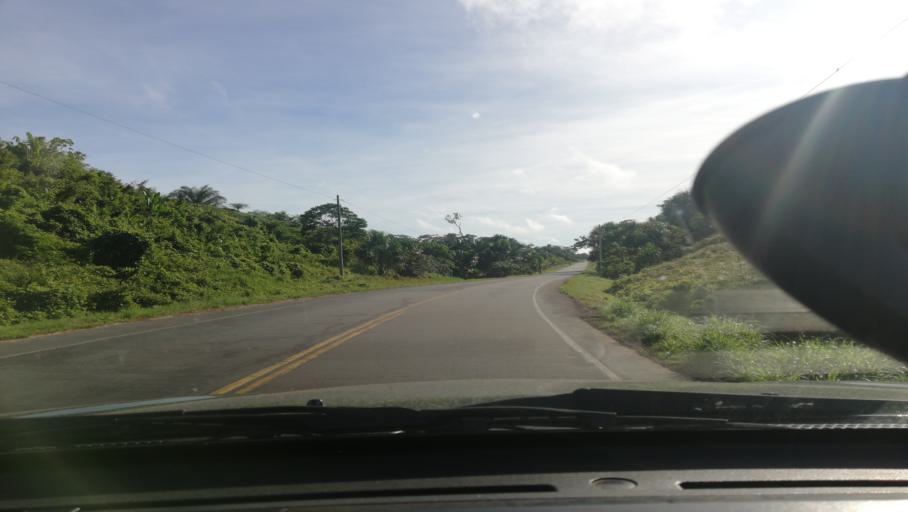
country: PE
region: Loreto
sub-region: Provincia de Loreto
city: Nauta
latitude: -4.3645
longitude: -73.5586
